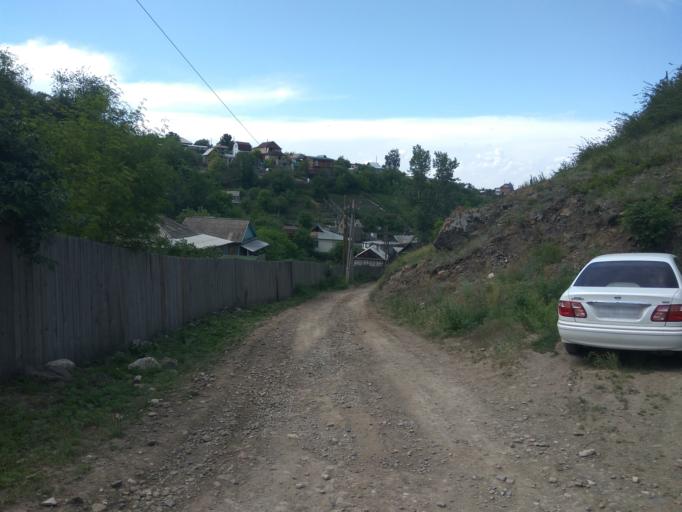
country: RU
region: Krasnoyarskiy
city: Krasnoyarsk
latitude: 55.9678
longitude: 92.8601
